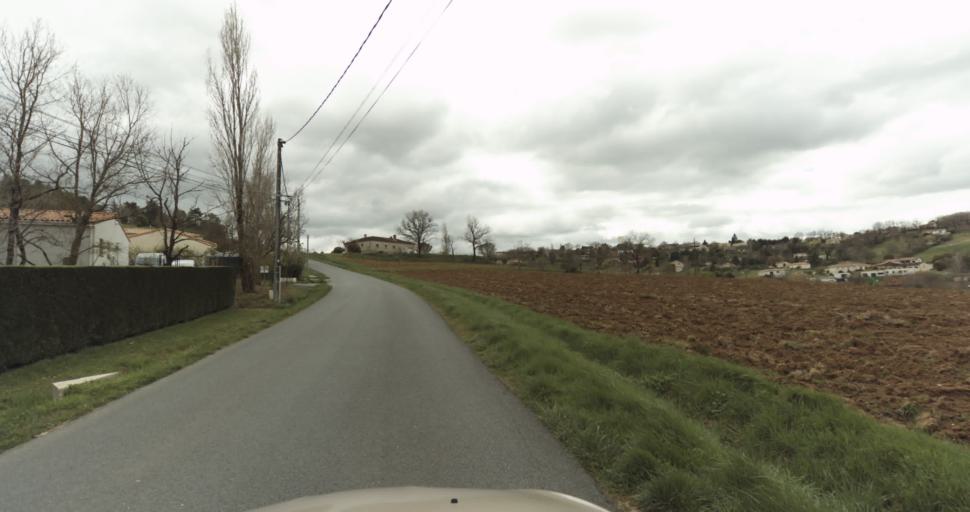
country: FR
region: Midi-Pyrenees
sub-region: Departement du Tarn
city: Puygouzon
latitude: 43.9058
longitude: 2.1724
